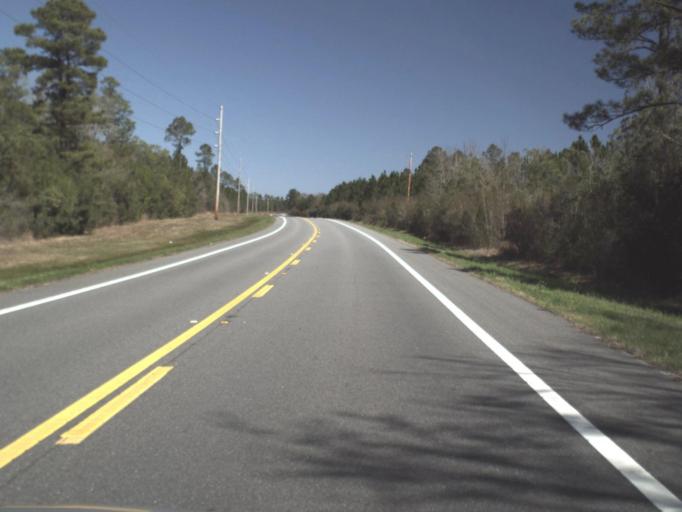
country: US
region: Florida
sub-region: Gadsden County
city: Quincy
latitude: 30.4029
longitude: -84.6724
